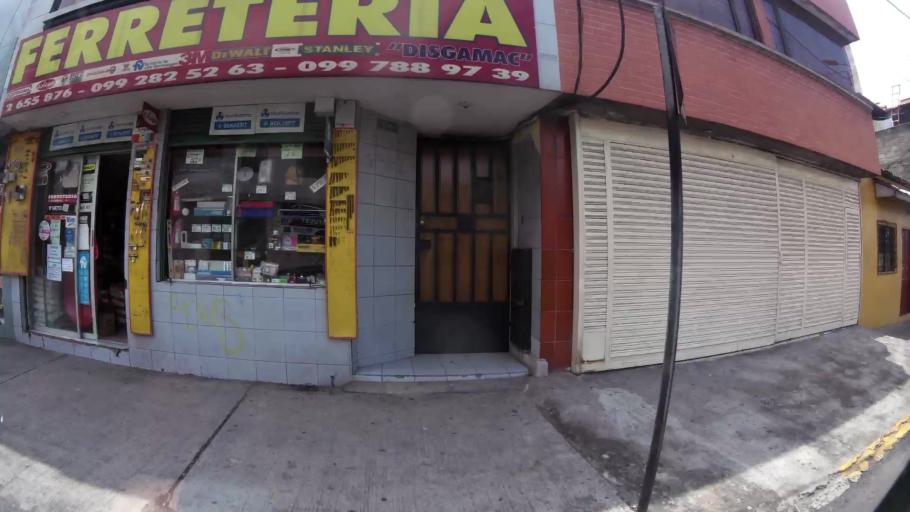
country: EC
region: Pichincha
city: Quito
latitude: -0.2553
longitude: -78.5214
